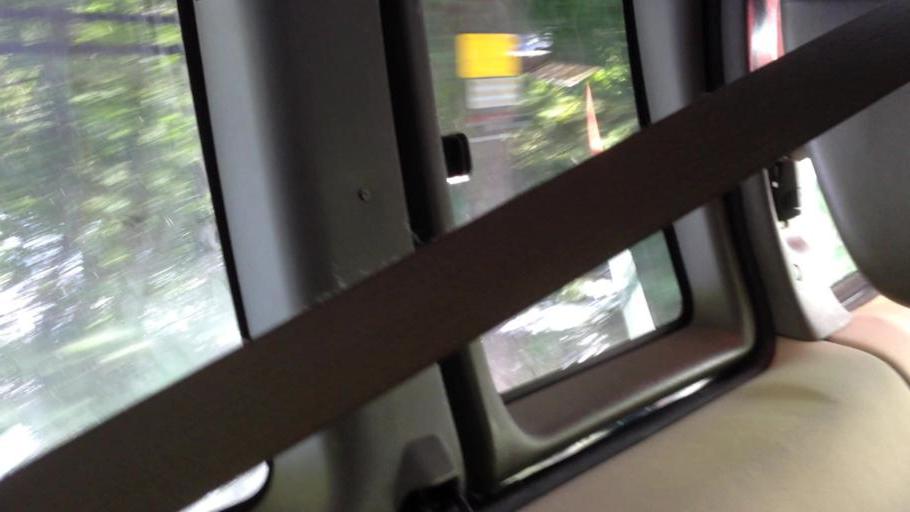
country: US
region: New York
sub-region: Dutchess County
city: Red Hook
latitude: 42.0057
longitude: -73.8804
